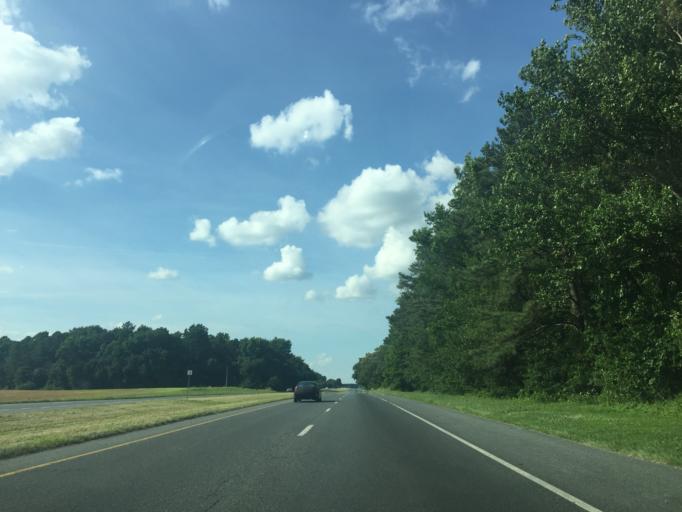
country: US
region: Delaware
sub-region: Sussex County
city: Bridgeville
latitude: 38.7675
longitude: -75.5927
